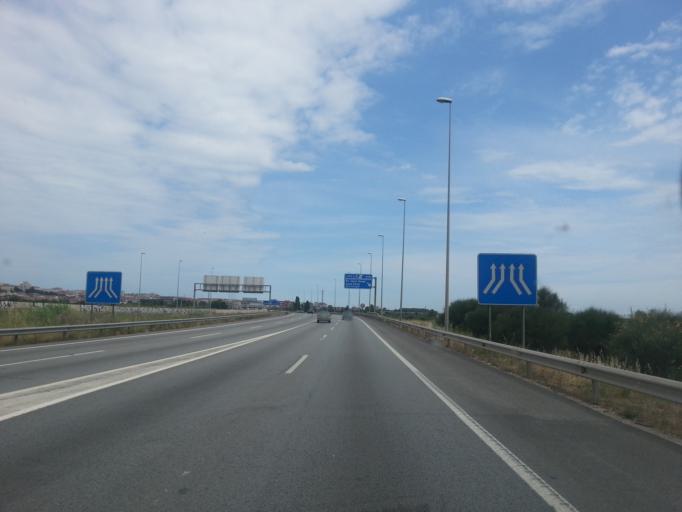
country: ES
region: Catalonia
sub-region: Provincia de Barcelona
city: Sant Feliu de Llobregat
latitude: 41.3710
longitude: 2.0385
